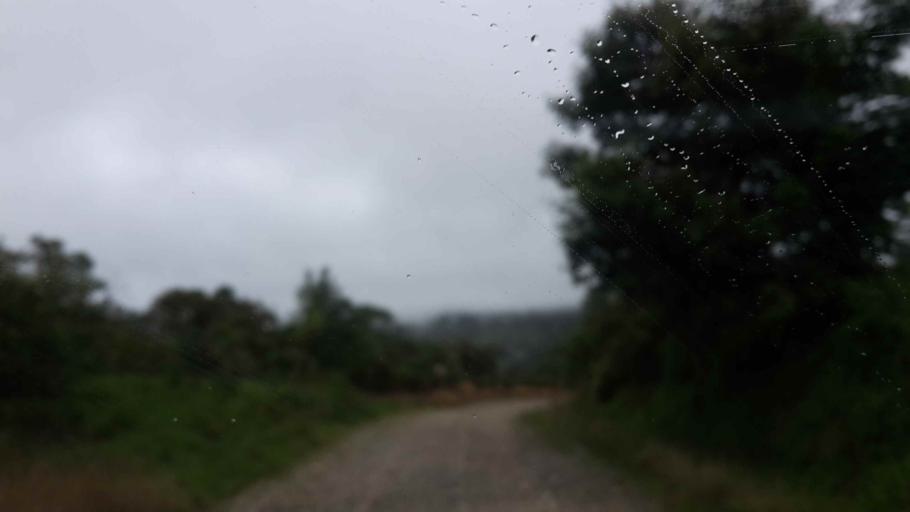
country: BO
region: Cochabamba
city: Colomi
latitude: -17.1368
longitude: -65.9415
